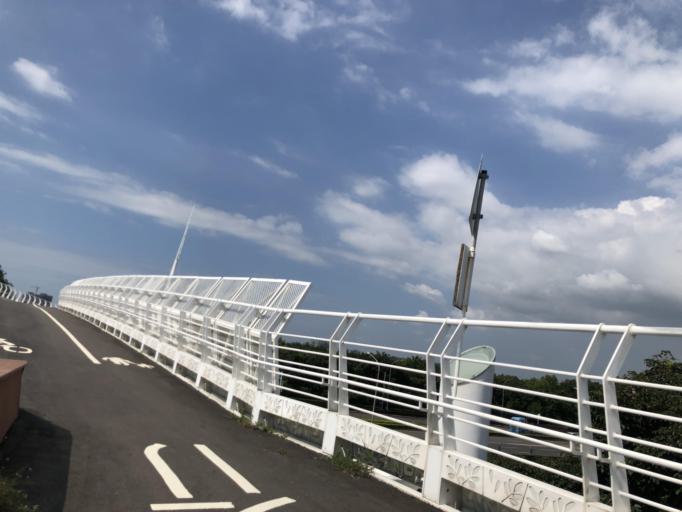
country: TW
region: Kaohsiung
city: Kaohsiung
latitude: 22.6792
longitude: 120.2992
